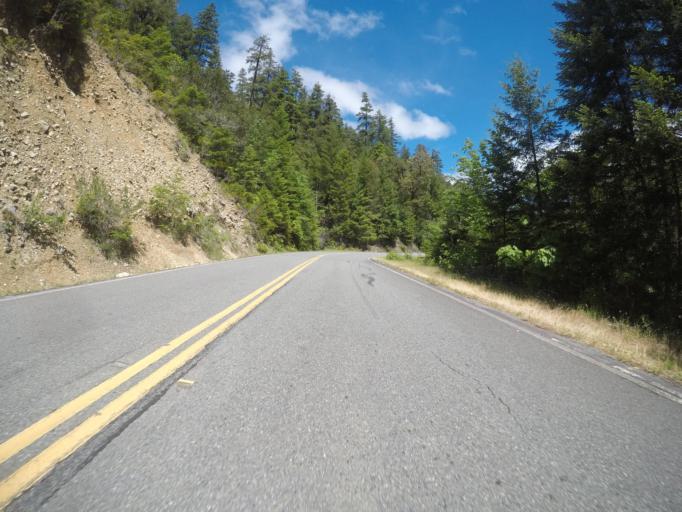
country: US
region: California
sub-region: Del Norte County
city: Bertsch-Oceanview
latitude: 41.7112
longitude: -123.9427
